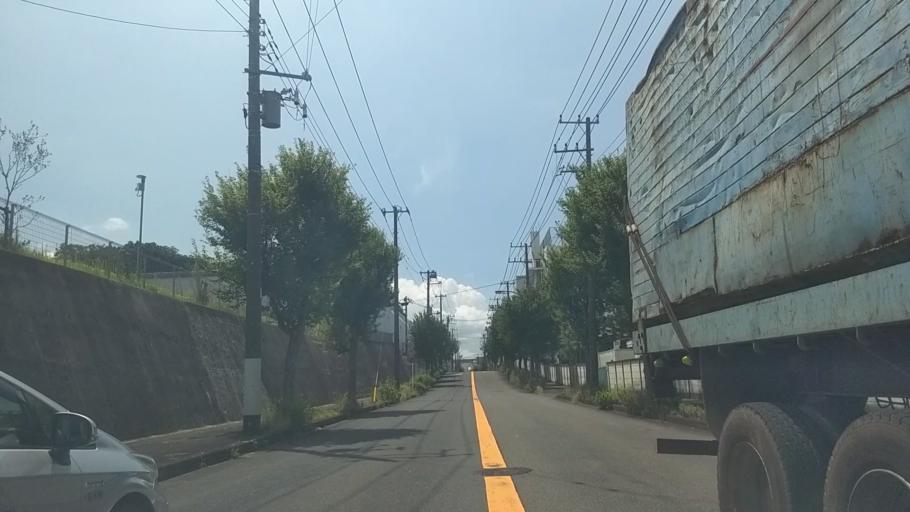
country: JP
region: Kanagawa
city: Yokosuka
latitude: 35.3163
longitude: 139.6409
